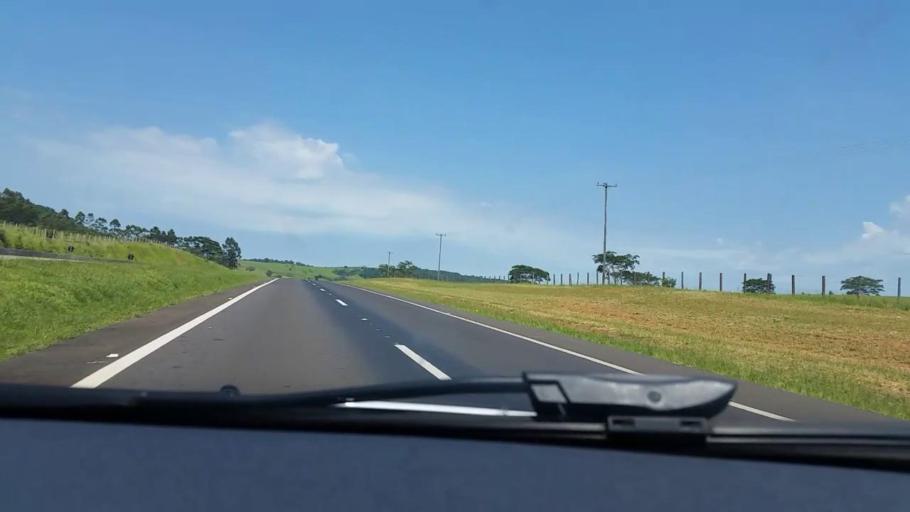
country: BR
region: Sao Paulo
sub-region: Bauru
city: Bauru
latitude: -22.4208
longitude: -49.1177
